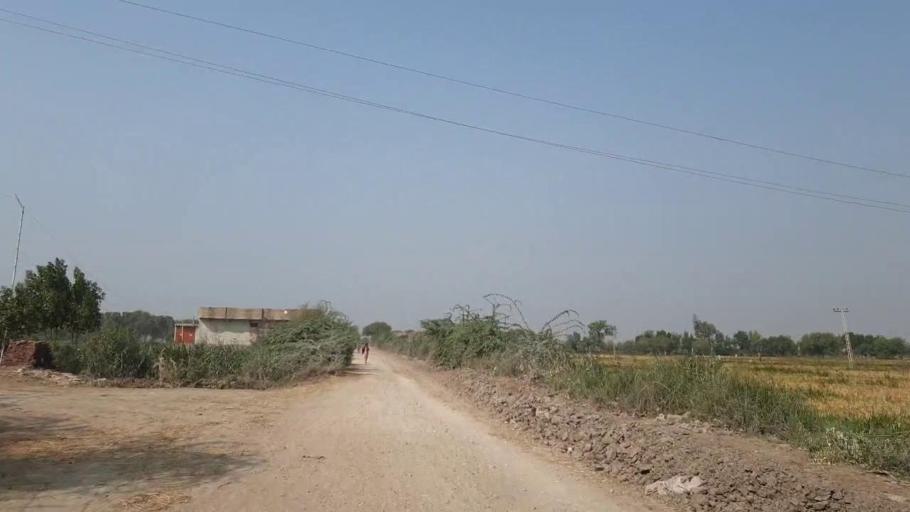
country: PK
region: Sindh
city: Kario
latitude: 24.9292
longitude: 68.5601
